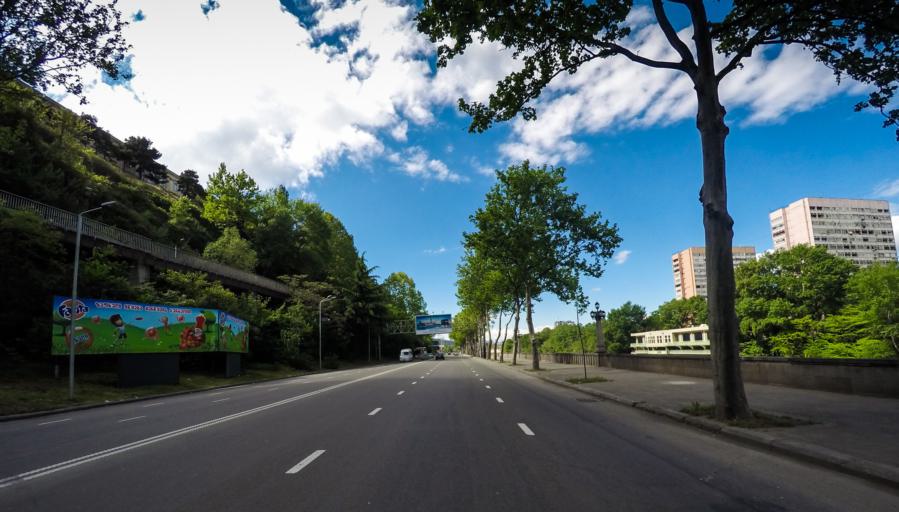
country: GE
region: T'bilisi
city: Tbilisi
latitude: 41.7175
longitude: 44.7862
